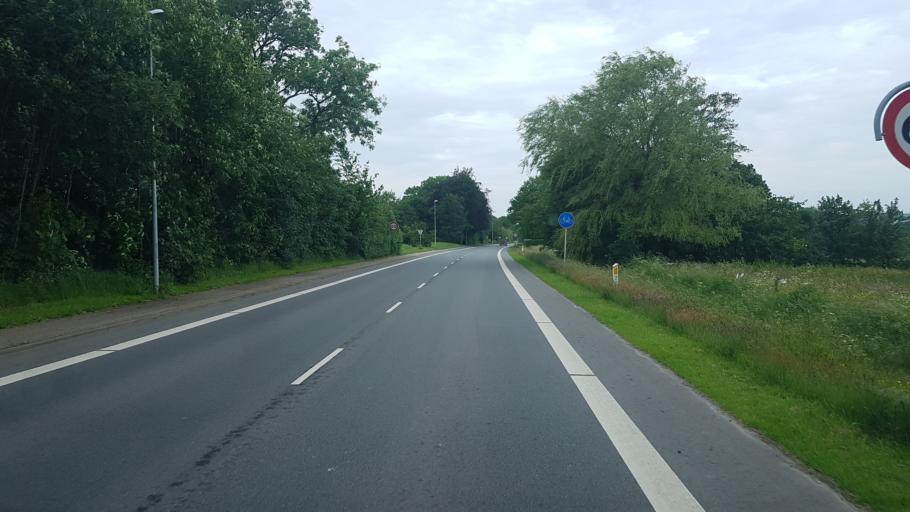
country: DK
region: South Denmark
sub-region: Vejen Kommune
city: Brorup
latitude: 55.4311
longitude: 9.0126
